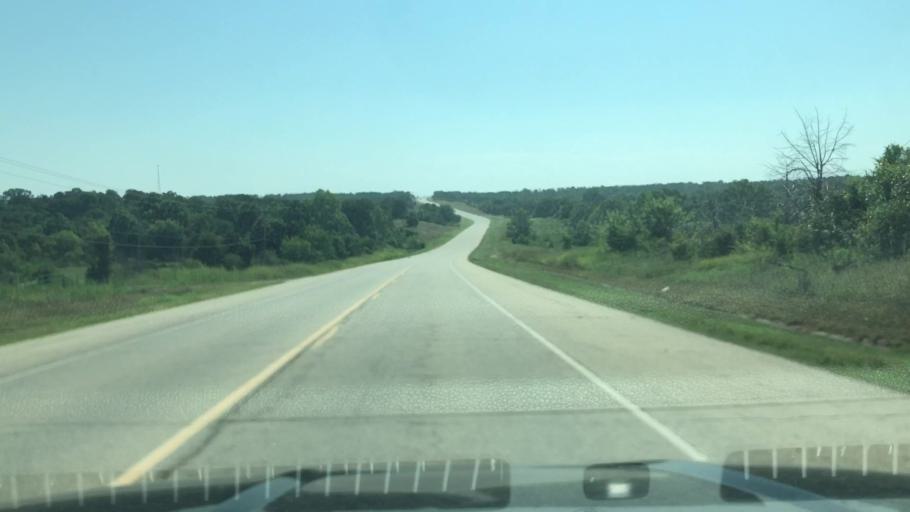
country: US
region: Oklahoma
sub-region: Creek County
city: Mannford
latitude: 36.0031
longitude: -96.4035
